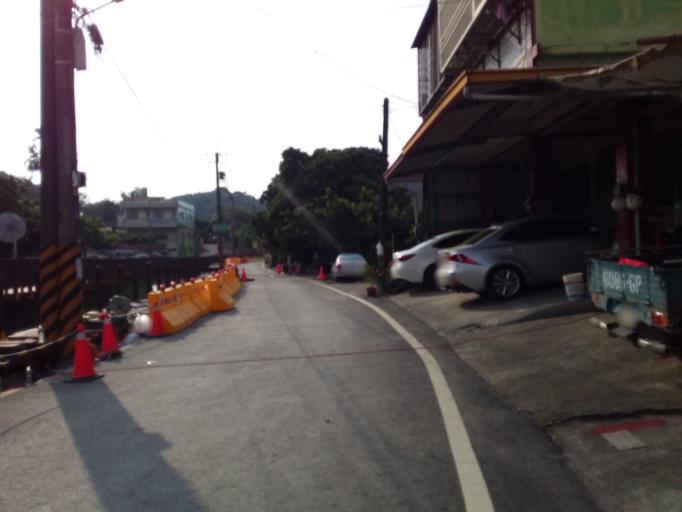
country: TW
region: Taiwan
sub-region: Pingtung
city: Pingtung
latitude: 22.6889
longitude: 120.4108
